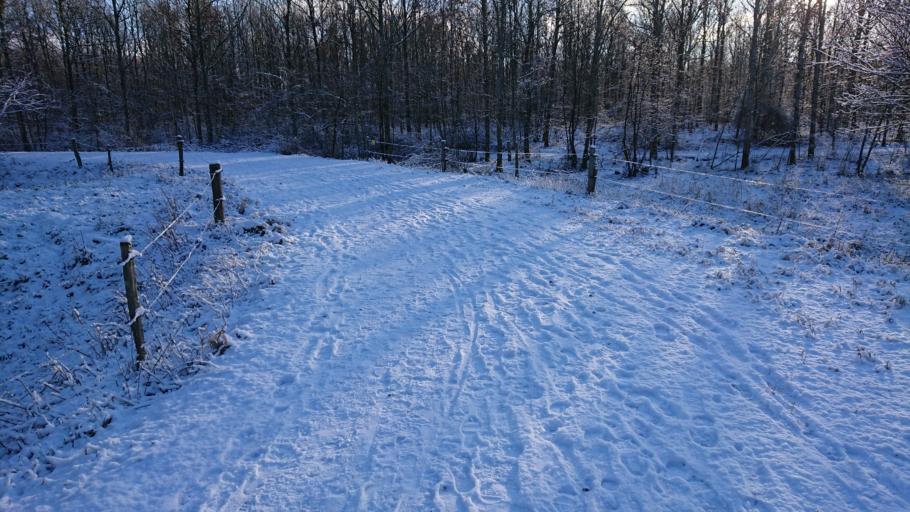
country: DK
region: Central Jutland
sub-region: Arhus Kommune
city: Stavtrup
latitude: 56.1721
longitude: 10.1010
